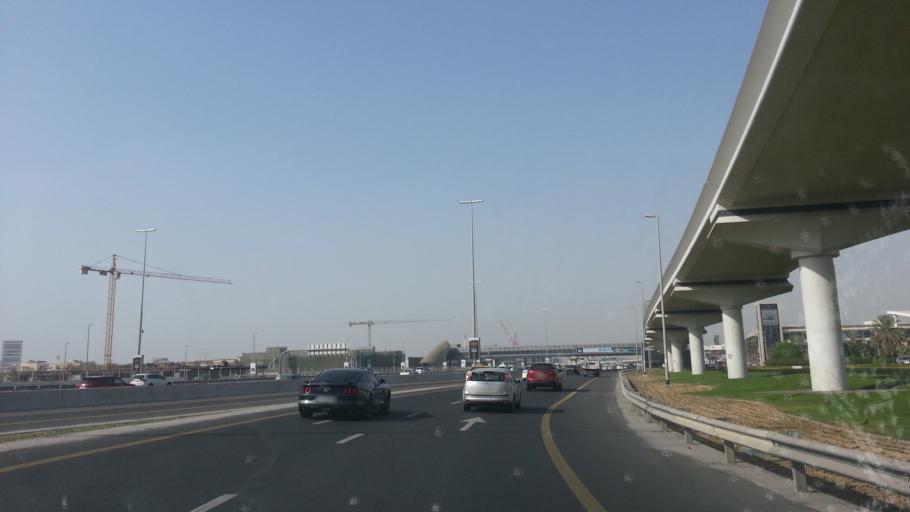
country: AE
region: Dubai
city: Dubai
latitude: 25.1240
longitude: 55.2042
